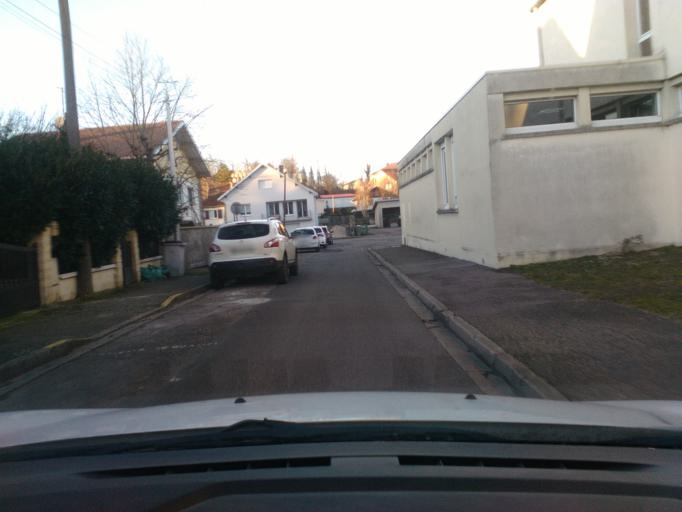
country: FR
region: Lorraine
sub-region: Departement des Vosges
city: Mirecourt
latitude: 48.2959
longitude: 6.1268
